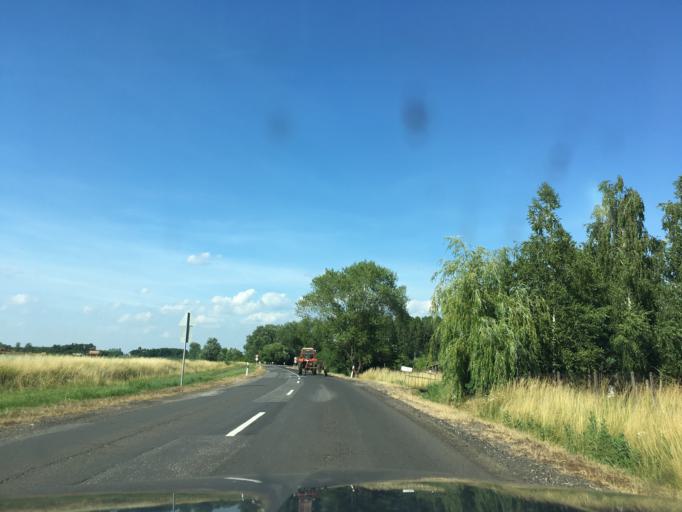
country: HU
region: Hajdu-Bihar
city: Hajdusamson
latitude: 47.5871
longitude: 21.7252
